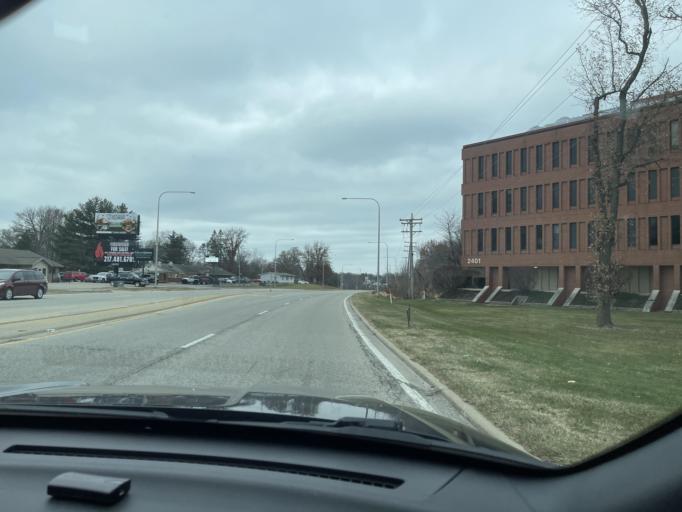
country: US
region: Illinois
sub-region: Sangamon County
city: Leland Grove
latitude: 39.8124
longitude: -89.6951
